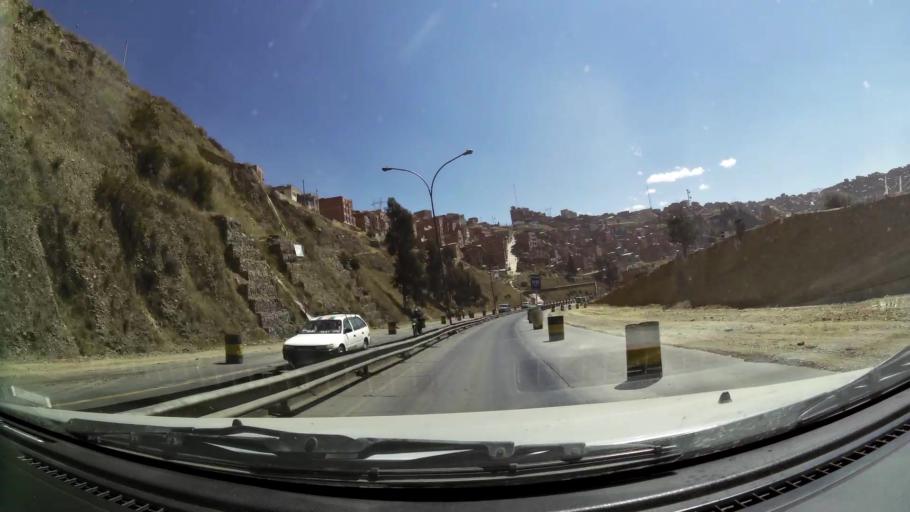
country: BO
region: La Paz
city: La Paz
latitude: -16.4928
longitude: -68.1684
